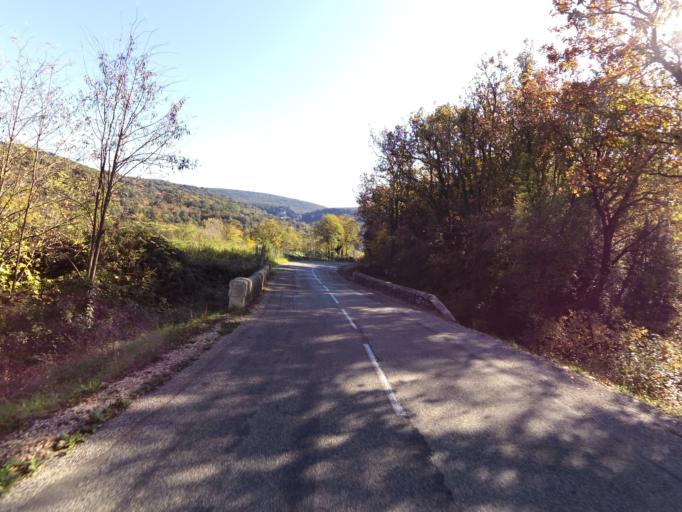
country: FR
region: Rhone-Alpes
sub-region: Departement de l'Ardeche
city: Ruoms
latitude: 44.4047
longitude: 4.4117
